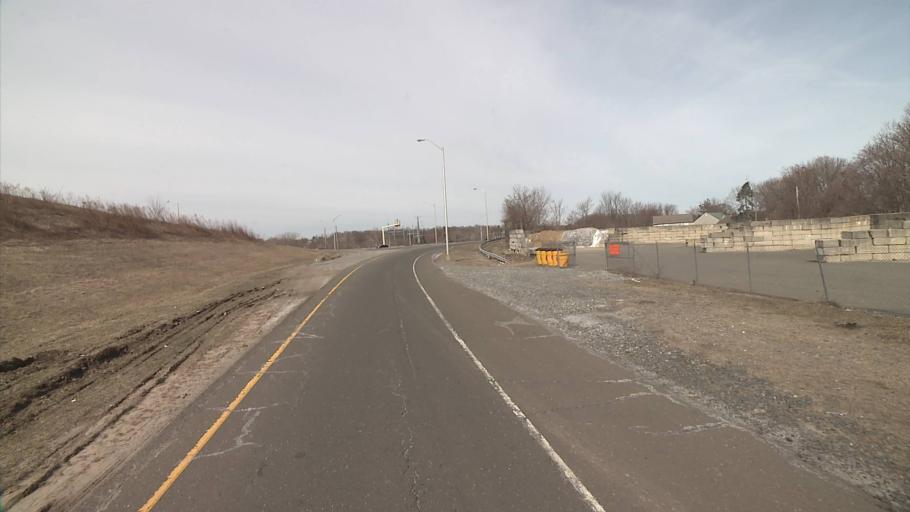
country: US
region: Connecticut
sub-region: Fairfield County
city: Norwalk
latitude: 41.1282
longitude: -73.4261
